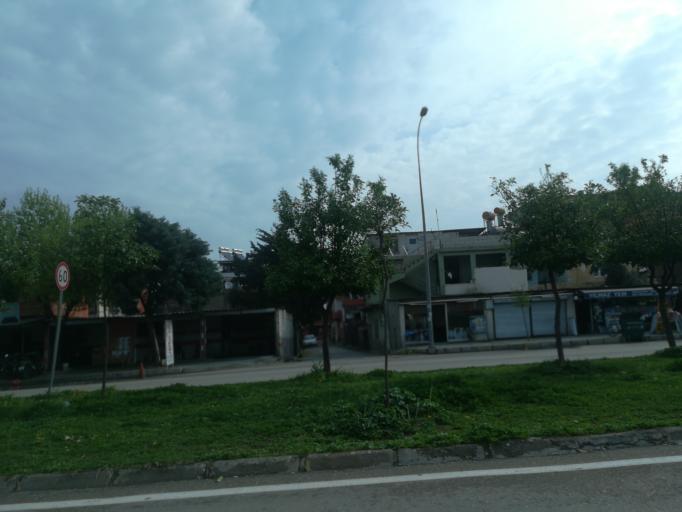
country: TR
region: Adana
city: Yuregir
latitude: 36.9976
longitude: 35.3578
